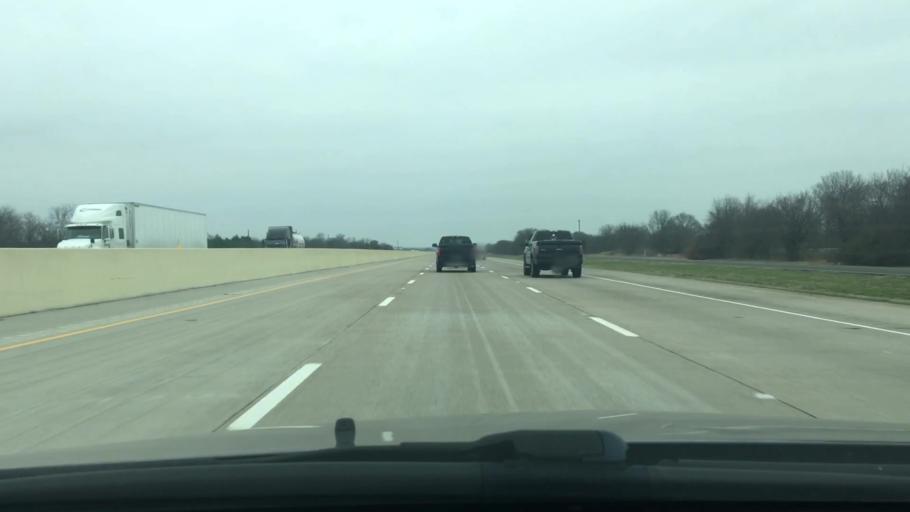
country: US
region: Texas
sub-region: Navarro County
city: Corsicana
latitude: 31.9821
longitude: -96.4239
